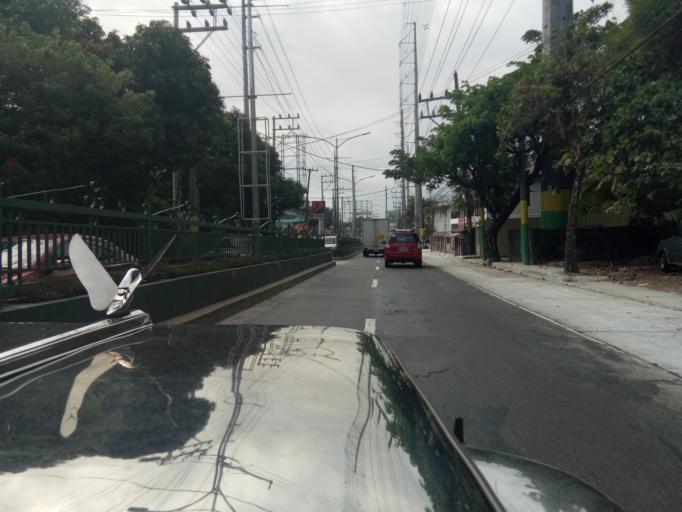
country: PH
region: Calabarzon
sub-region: Province of Cavite
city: Dasmarinas
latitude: 14.3156
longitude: 120.9449
